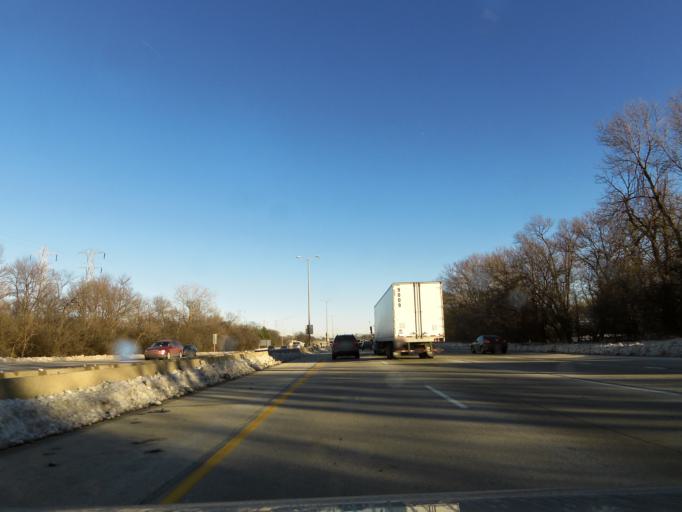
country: US
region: Wisconsin
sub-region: Milwaukee County
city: Greenfield
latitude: 42.9624
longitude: -87.9946
